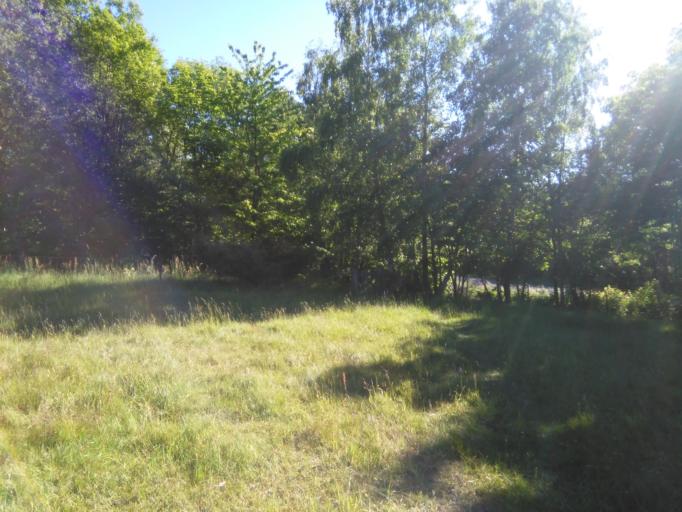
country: DK
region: Capital Region
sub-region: Bornholm Kommune
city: Ronne
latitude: 55.2604
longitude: 14.7655
